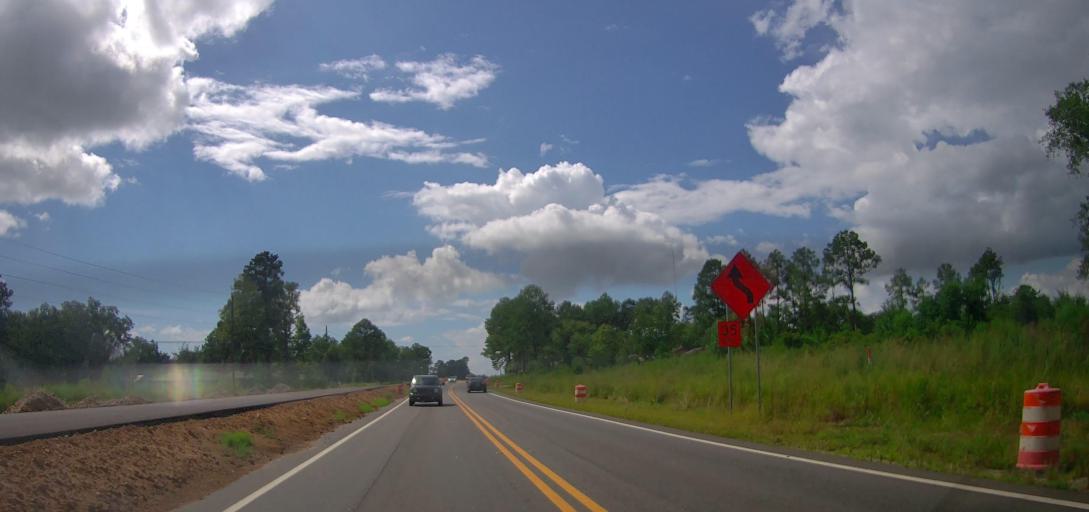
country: US
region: Georgia
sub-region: Coffee County
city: Douglas
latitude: 31.5272
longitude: -82.9055
